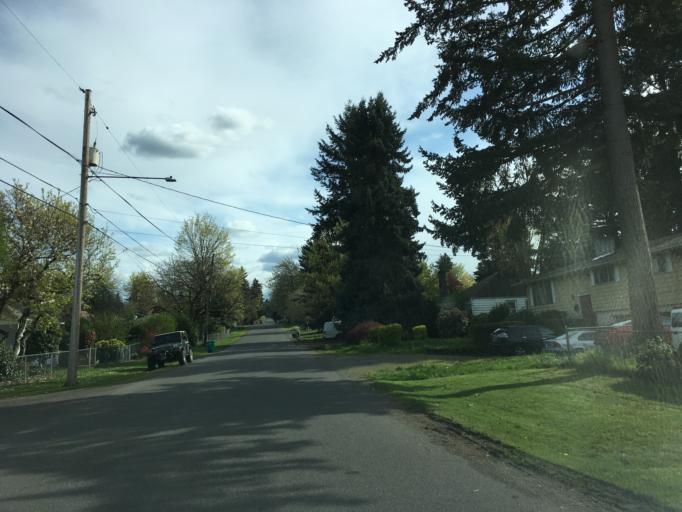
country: US
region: Oregon
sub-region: Multnomah County
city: Lents
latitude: 45.5552
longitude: -122.5507
